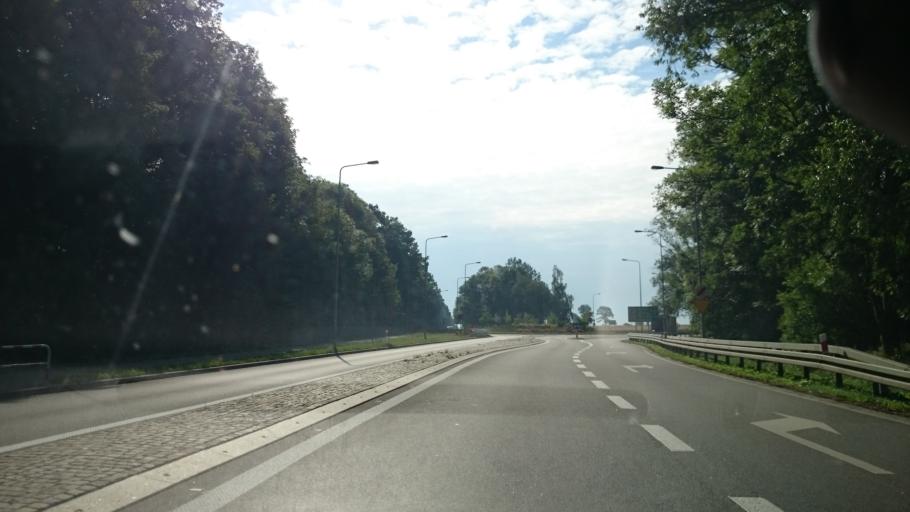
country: PL
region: Opole Voivodeship
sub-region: Powiat strzelecki
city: Strzelce Opolskie
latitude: 50.5028
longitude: 18.3345
